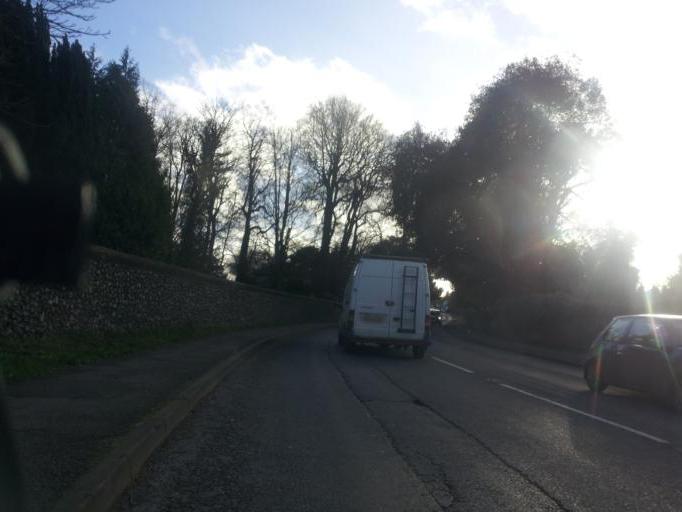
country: GB
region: England
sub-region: Kent
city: Meopham
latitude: 51.3718
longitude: 0.3608
